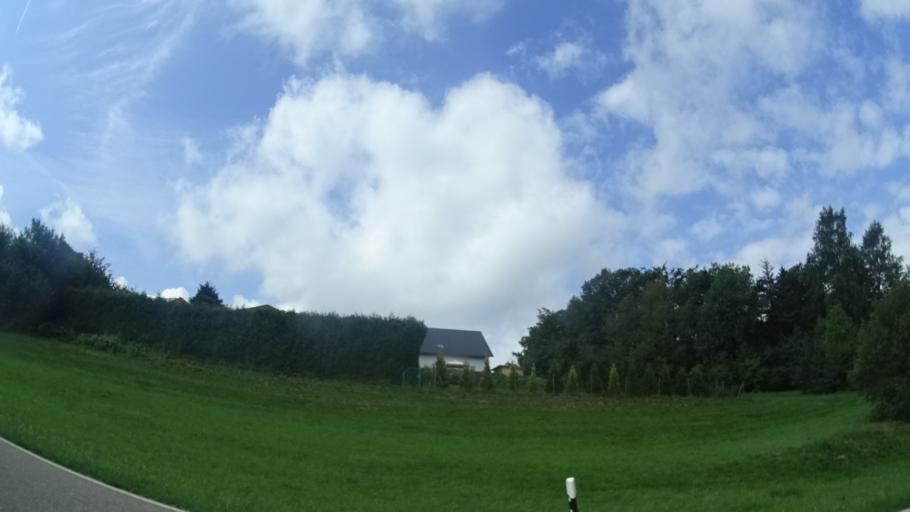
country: DE
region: Baden-Wuerttemberg
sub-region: Karlsruhe Region
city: Dobel
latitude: 48.8007
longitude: 8.4895
